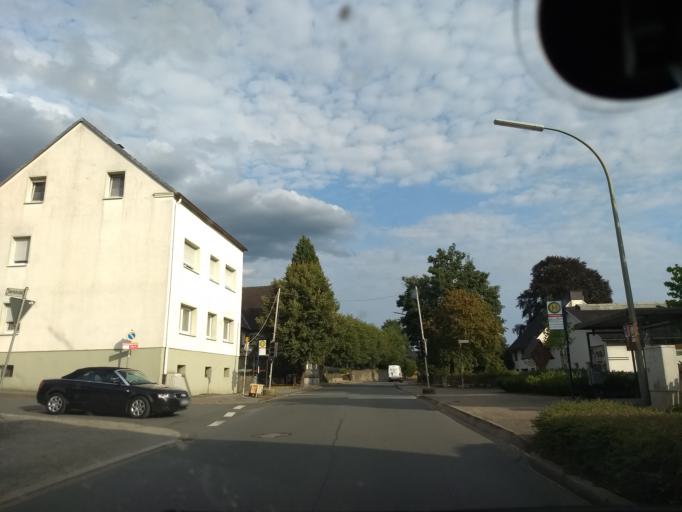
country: DE
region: North Rhine-Westphalia
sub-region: Regierungsbezirk Arnsberg
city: Arnsberg
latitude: 51.4018
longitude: 8.0870
